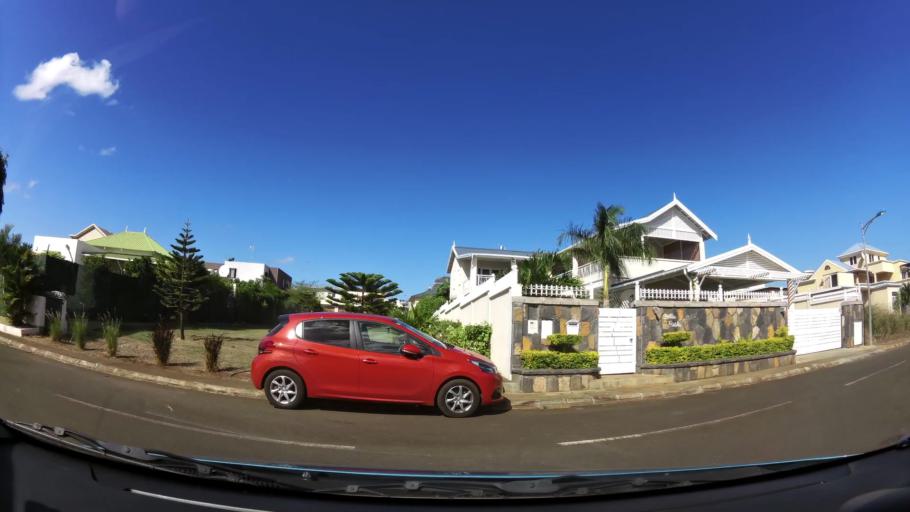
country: MU
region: Black River
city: Albion
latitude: -20.2174
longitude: 57.4102
